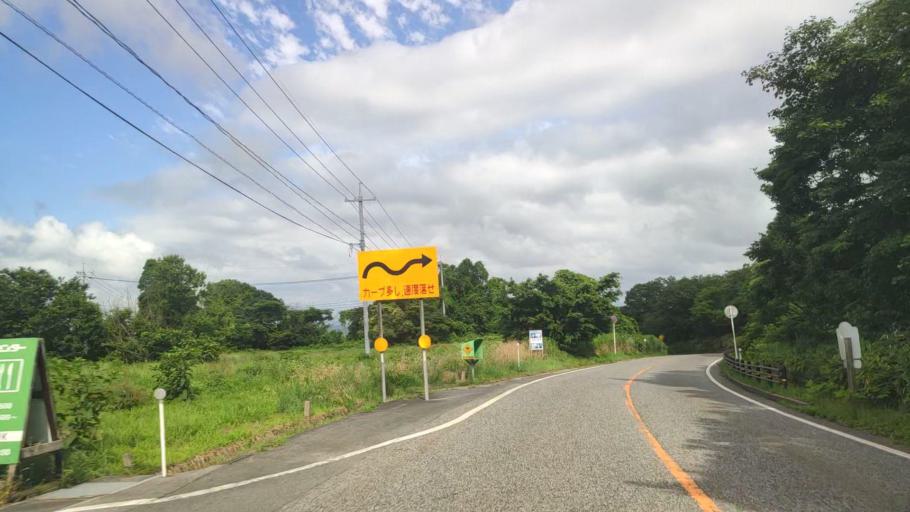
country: JP
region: Tottori
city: Yonago
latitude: 35.4140
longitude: 133.4657
